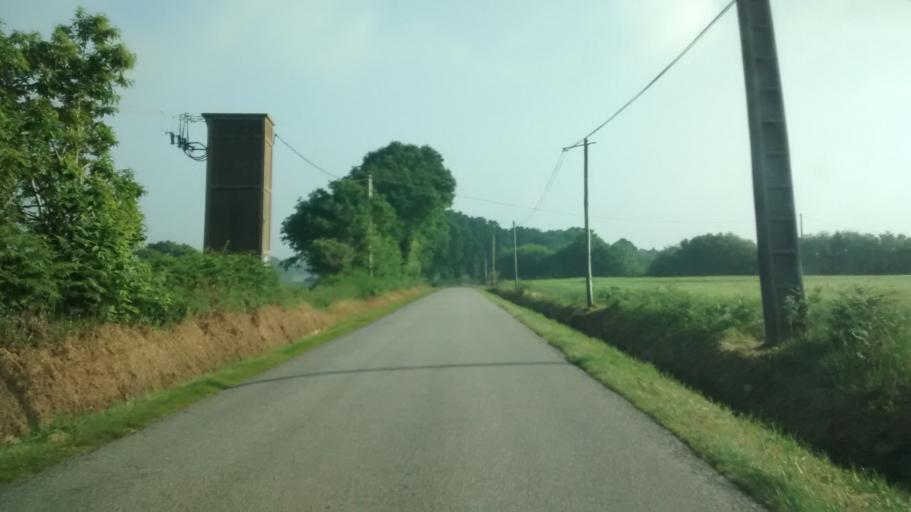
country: FR
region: Brittany
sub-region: Departement du Morbihan
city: Ruffiac
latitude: 47.8329
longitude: -2.2770
